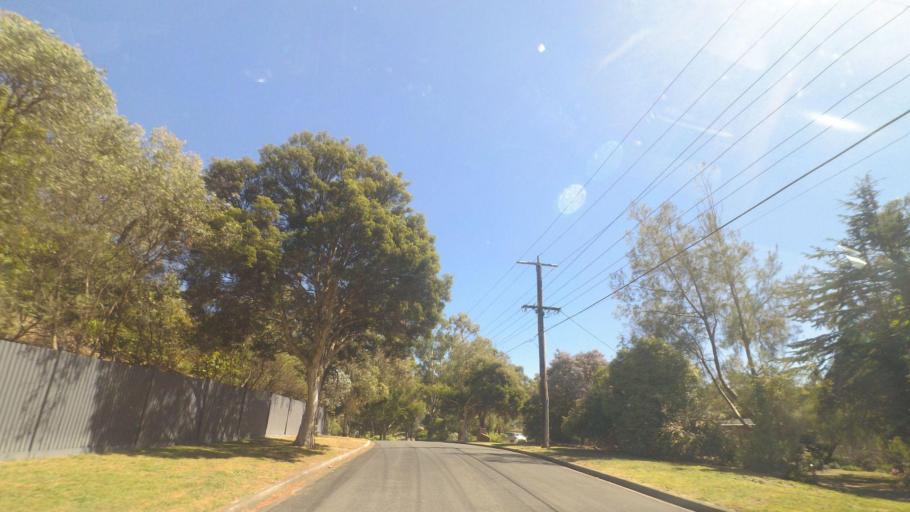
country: AU
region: Victoria
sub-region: Manningham
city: Donvale
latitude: -37.7923
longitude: 145.1934
